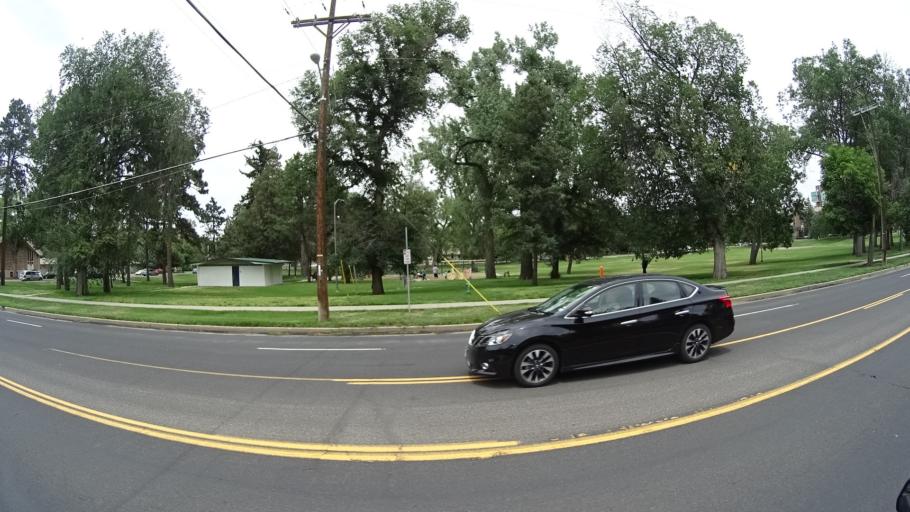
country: US
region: Colorado
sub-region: El Paso County
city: Colorado Springs
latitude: 38.8388
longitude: -104.8029
